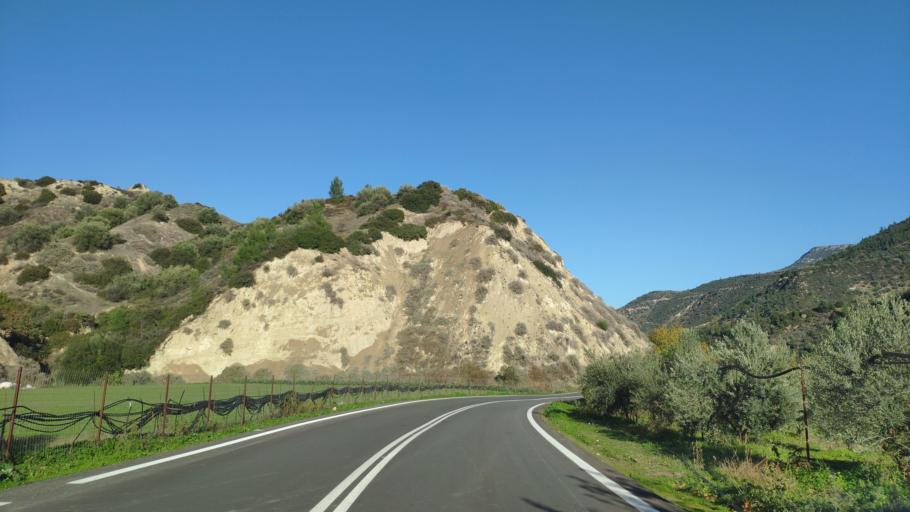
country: GR
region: Peloponnese
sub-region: Nomos Korinthias
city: Xylokastro
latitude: 38.0143
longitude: 22.5475
